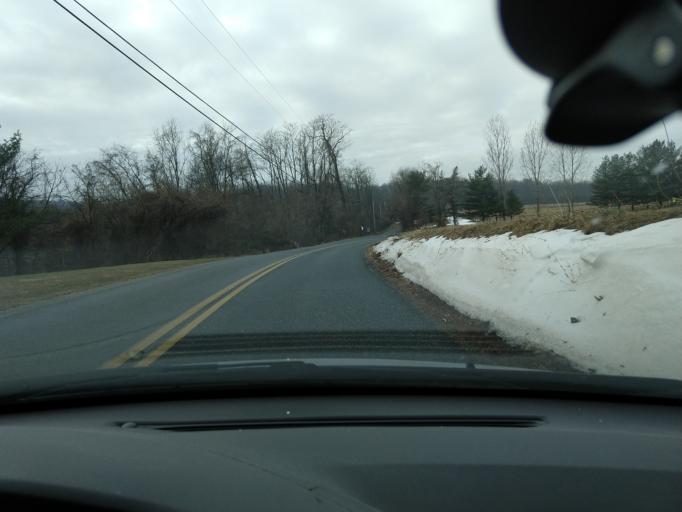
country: US
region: Pennsylvania
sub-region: Berks County
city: Amity Gardens
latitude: 40.2376
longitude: -75.7511
